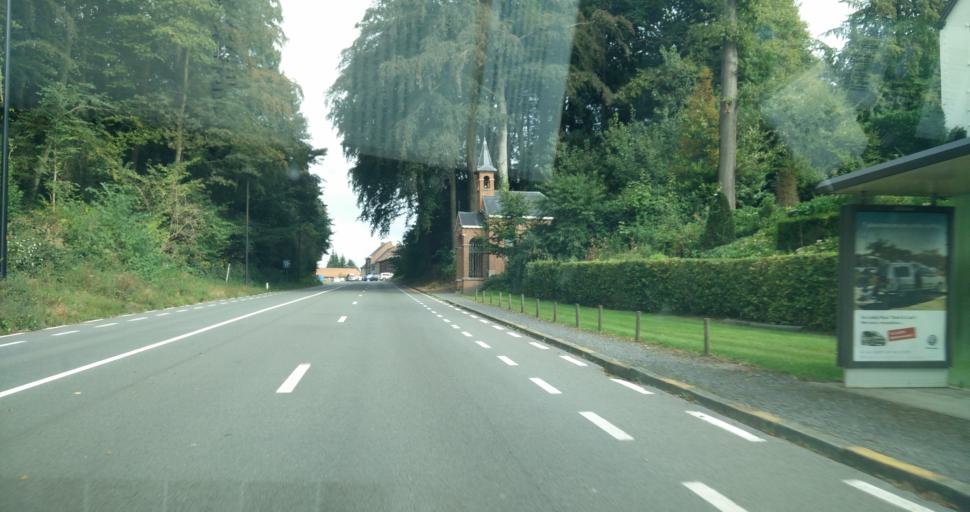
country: BE
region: Flanders
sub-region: Provincie Oost-Vlaanderen
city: Ronse
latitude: 50.7603
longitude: 3.5873
